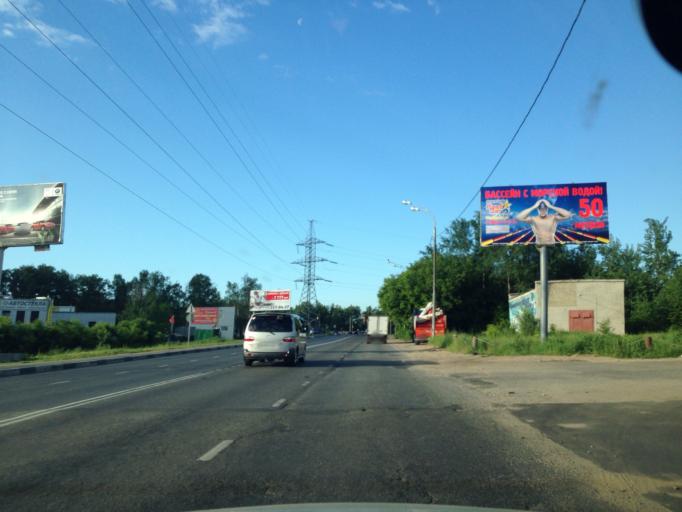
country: RU
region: Moscow
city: Vostochnyy
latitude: 55.7927
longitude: 37.8952
